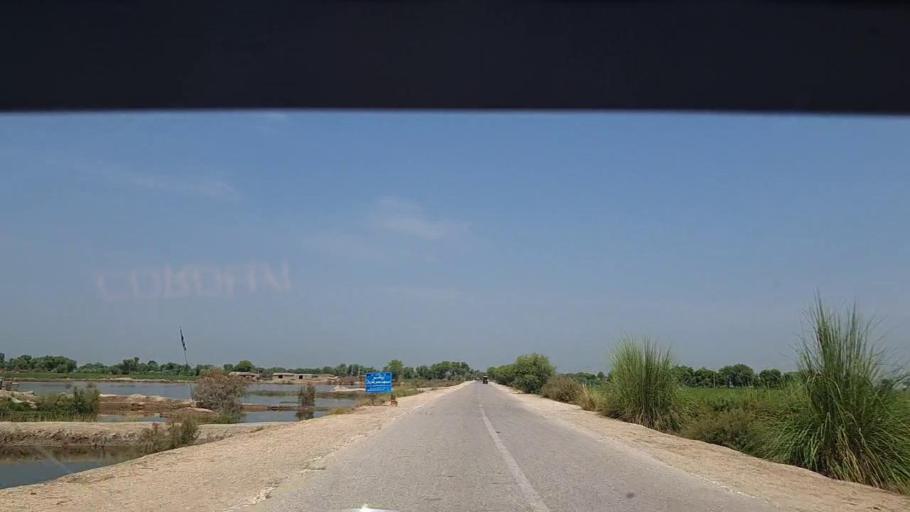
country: PK
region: Sindh
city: Thul
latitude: 28.1387
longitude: 68.8175
